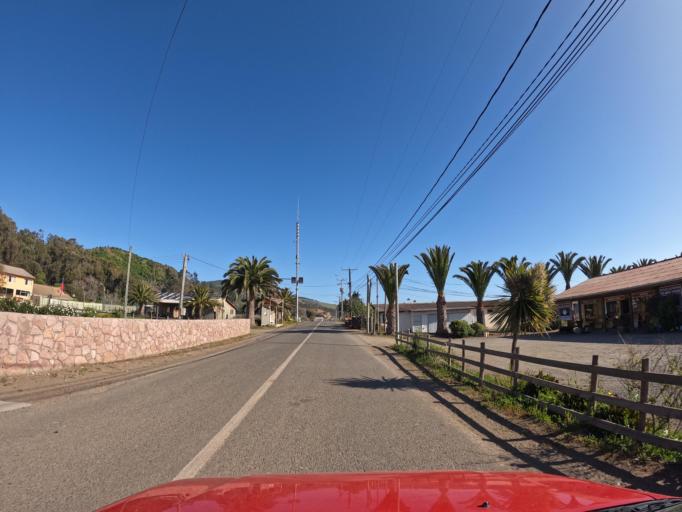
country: CL
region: Maule
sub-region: Provincia de Talca
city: Constitucion
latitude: -34.8447
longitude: -72.1414
